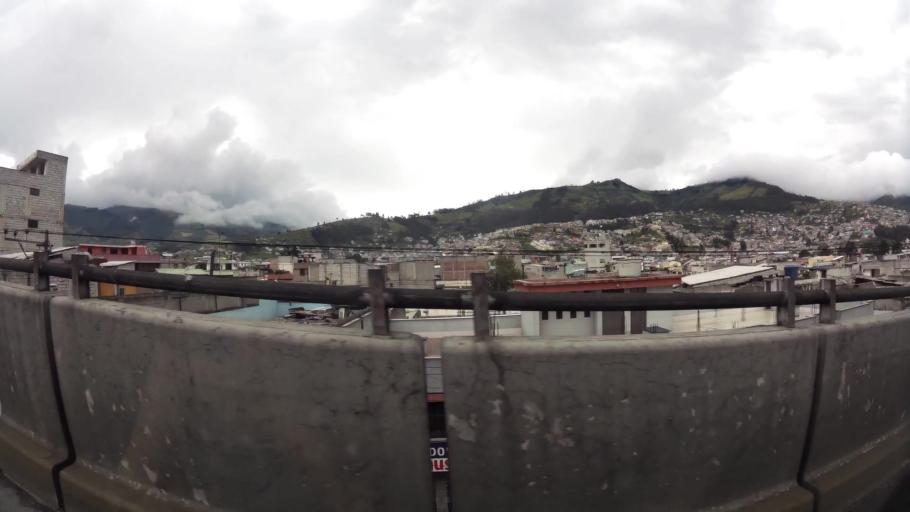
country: EC
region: Pichincha
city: Quito
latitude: -0.2782
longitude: -78.5528
